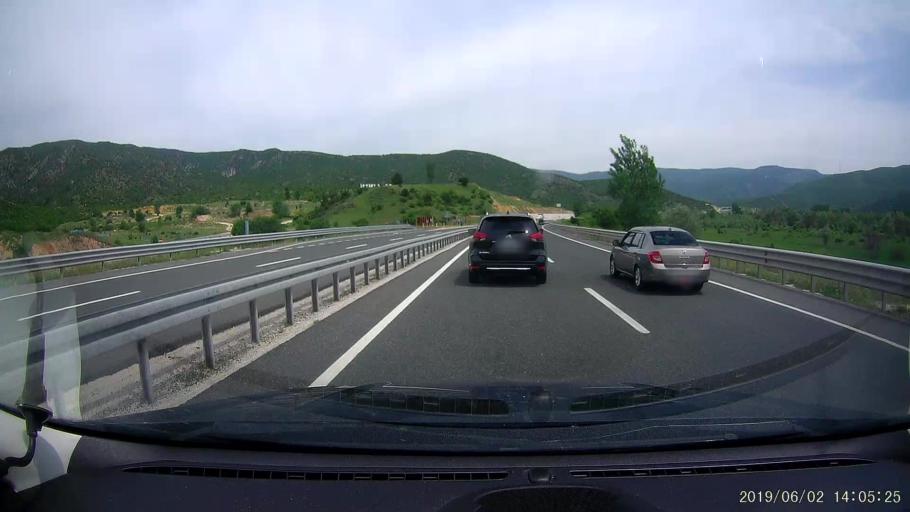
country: TR
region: Cankiri
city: Ilgaz
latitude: 40.9014
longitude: 33.6684
